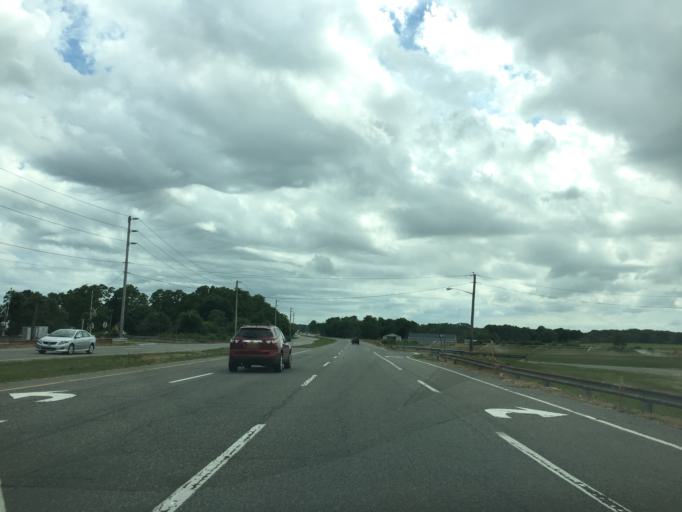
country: US
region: New York
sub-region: Suffolk County
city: Mattituck
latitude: 41.0019
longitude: -72.5264
